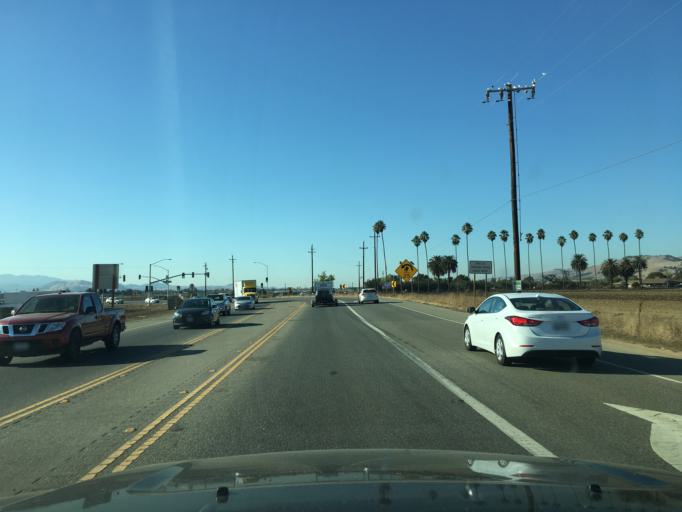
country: US
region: California
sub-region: Santa Clara County
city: Gilroy
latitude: 37.0090
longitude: -121.5144
